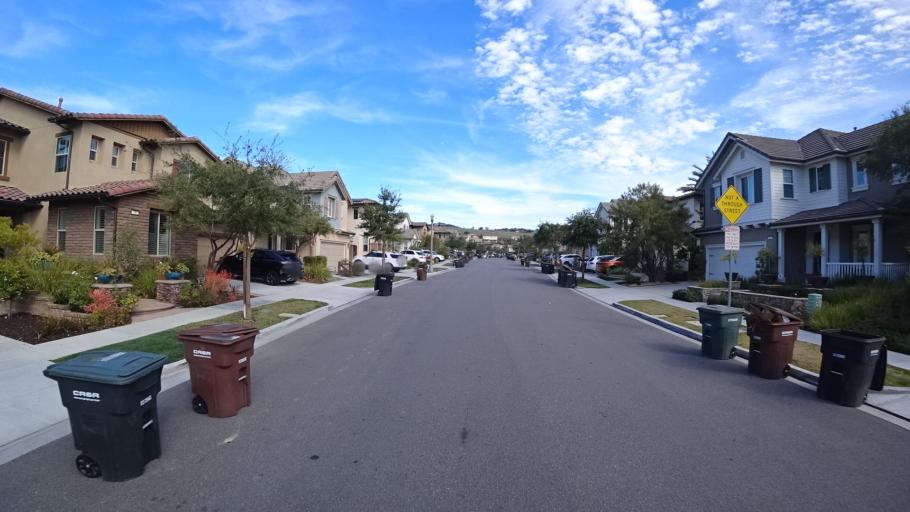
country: US
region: California
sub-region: Orange County
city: Ladera Ranch
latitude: 33.5281
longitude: -117.6251
